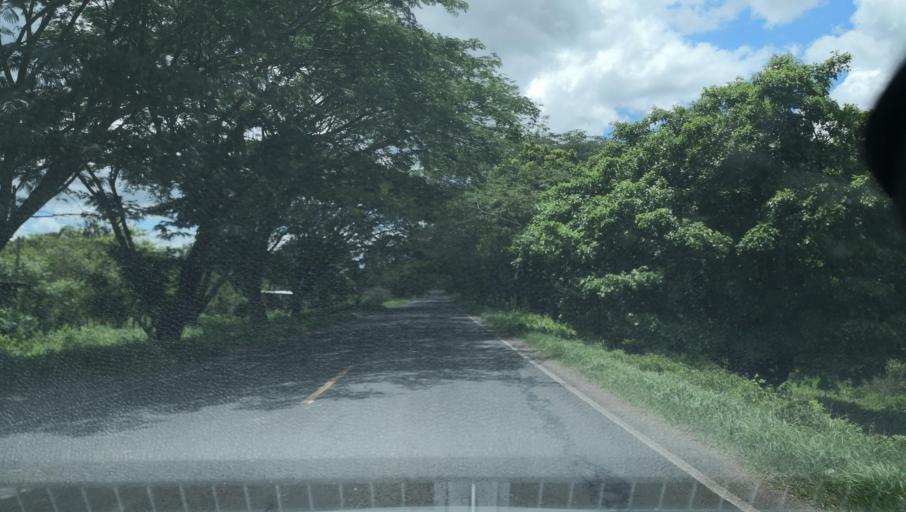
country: NI
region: Madriz
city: Palacaguina
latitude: 13.4262
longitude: -86.4047
